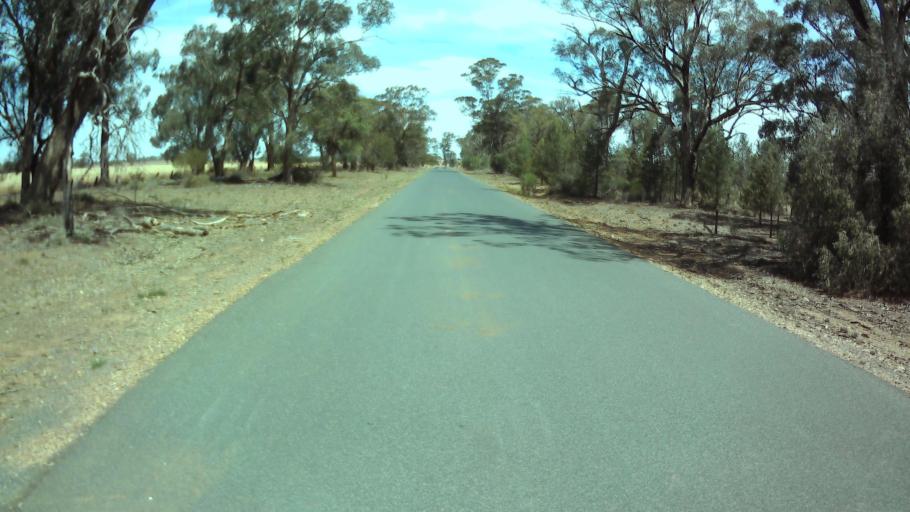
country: AU
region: New South Wales
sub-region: Weddin
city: Grenfell
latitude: -33.8548
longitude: 147.7455
